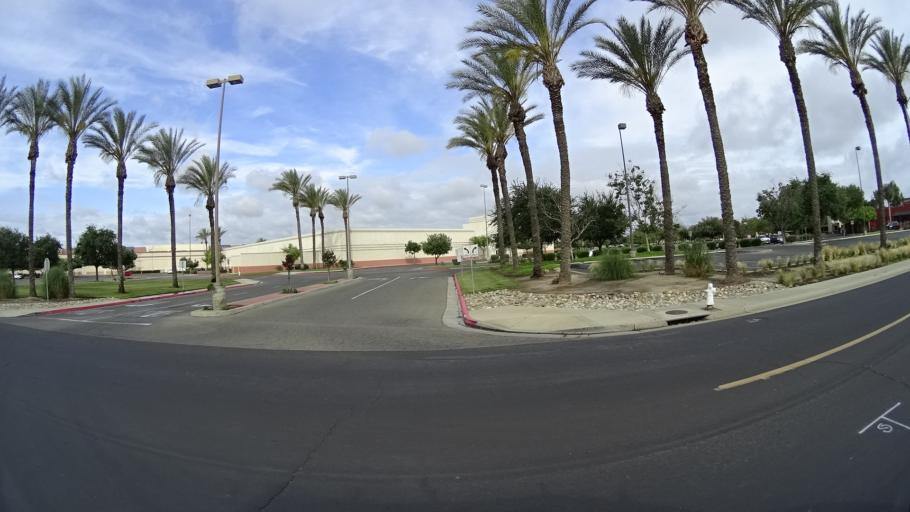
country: US
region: California
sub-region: Kings County
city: Hanford
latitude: 36.3268
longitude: -119.6685
